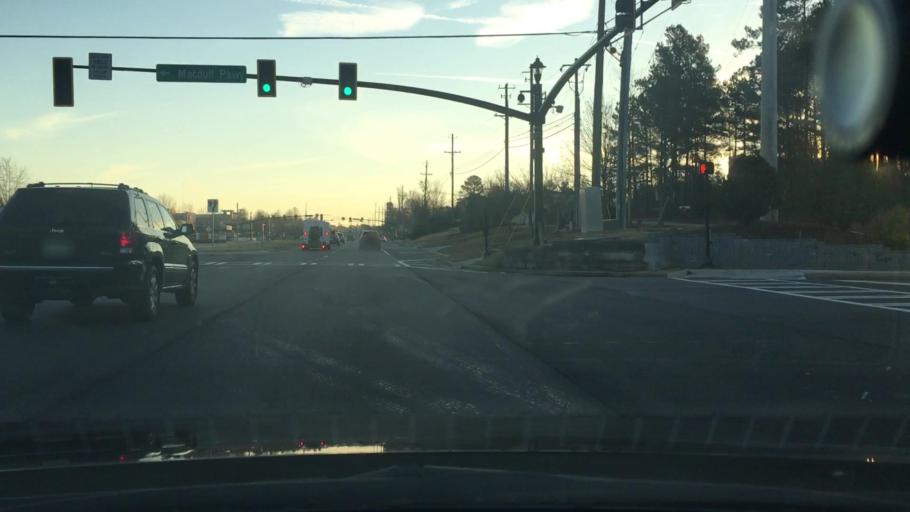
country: US
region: Georgia
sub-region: Fayette County
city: Peachtree City
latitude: 33.3968
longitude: -84.6043
